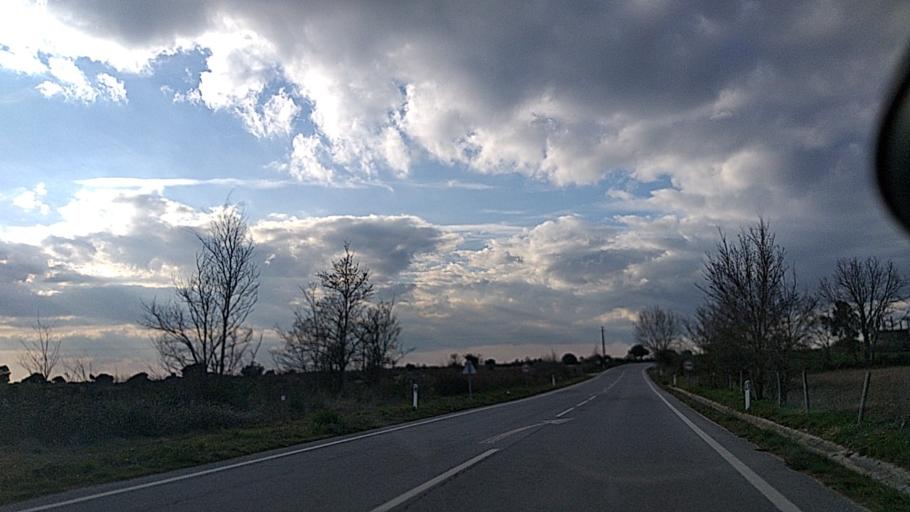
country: ES
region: Castille and Leon
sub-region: Provincia de Salamanca
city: Aldea del Obispo
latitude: 40.6972
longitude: -6.8865
